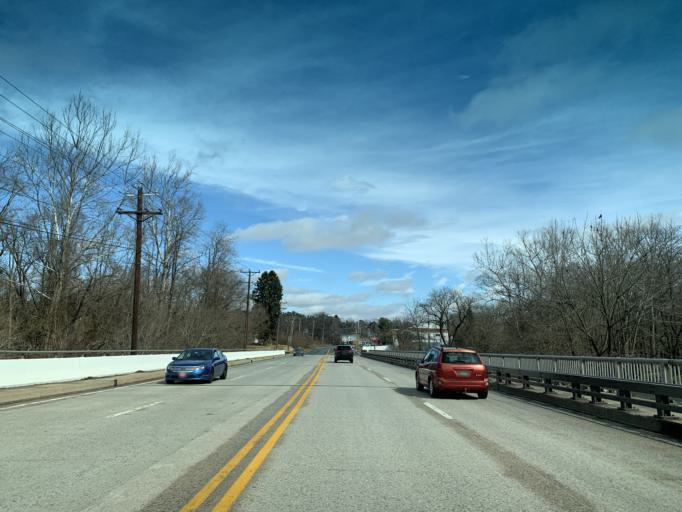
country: US
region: Delaware
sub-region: New Castle County
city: Brookside
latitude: 39.6922
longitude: -75.7247
